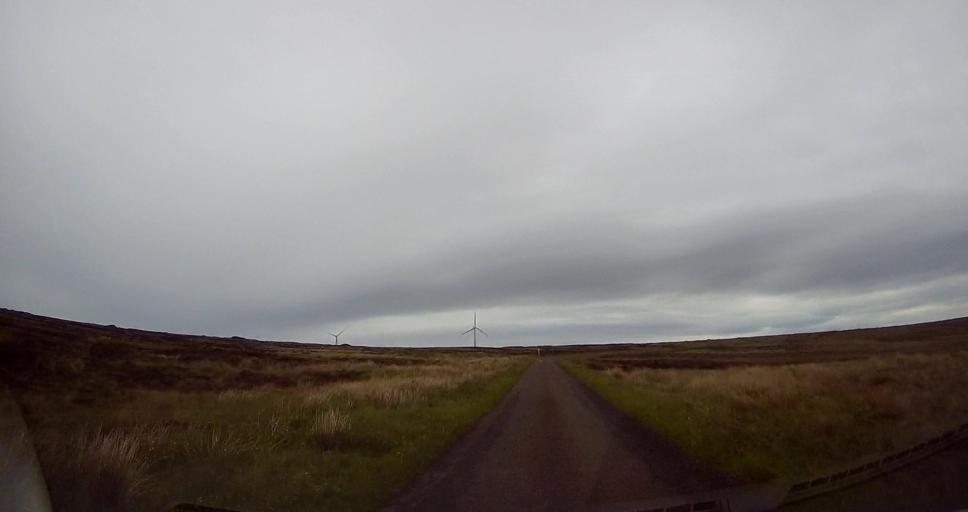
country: GB
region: Scotland
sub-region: Orkney Islands
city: Stromness
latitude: 59.0993
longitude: -3.1494
